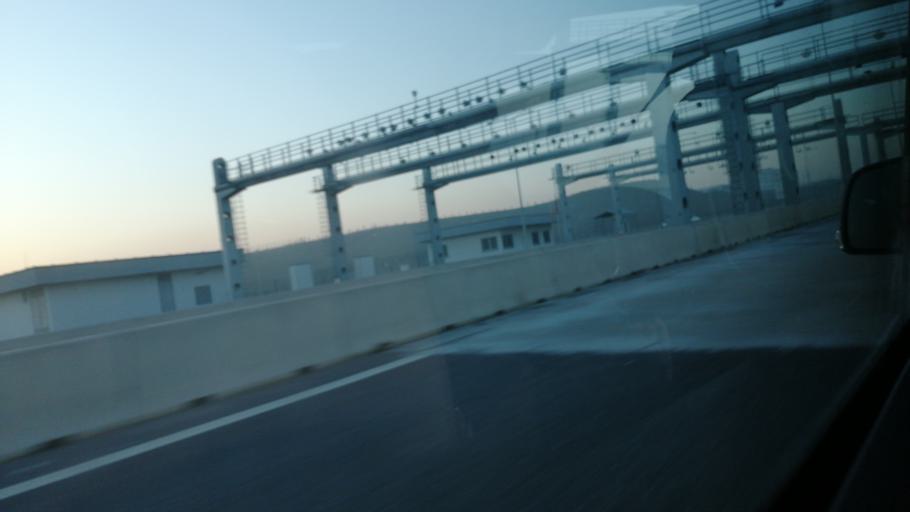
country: TR
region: Kocaeli
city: Tavsanli
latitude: 40.7848
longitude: 29.5160
